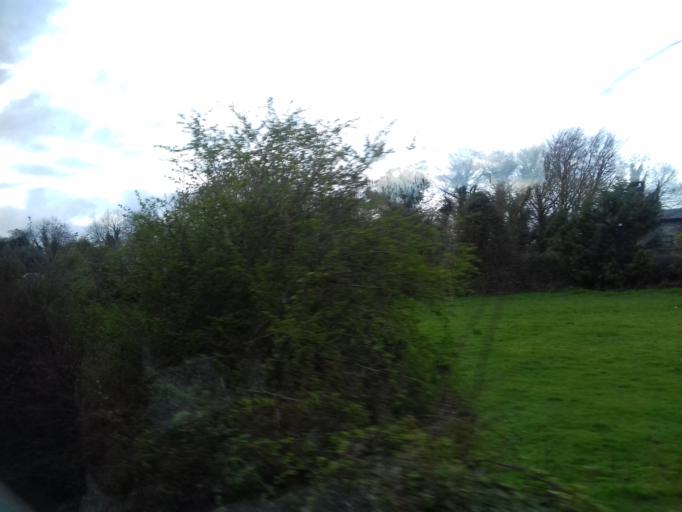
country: IE
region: Leinster
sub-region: An Iarmhi
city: Rathwire
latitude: 53.4937
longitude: -7.1577
